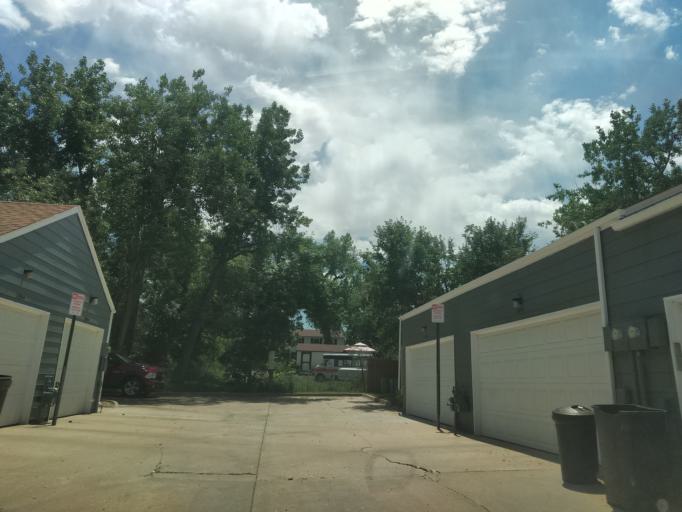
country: US
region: Colorado
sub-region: Jefferson County
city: Lakewood
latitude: 39.6806
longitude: -105.0869
